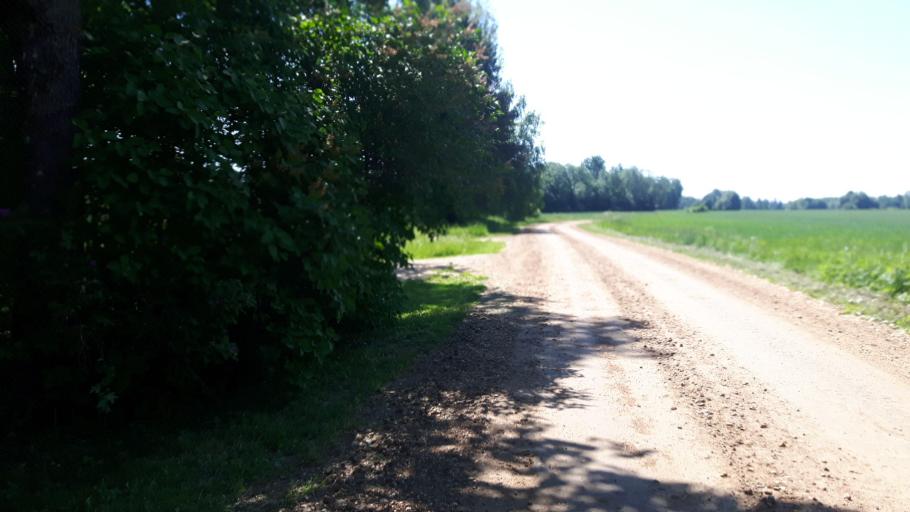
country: EE
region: Paernumaa
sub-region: Tootsi vald
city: Tootsi
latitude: 58.5030
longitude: 24.9061
